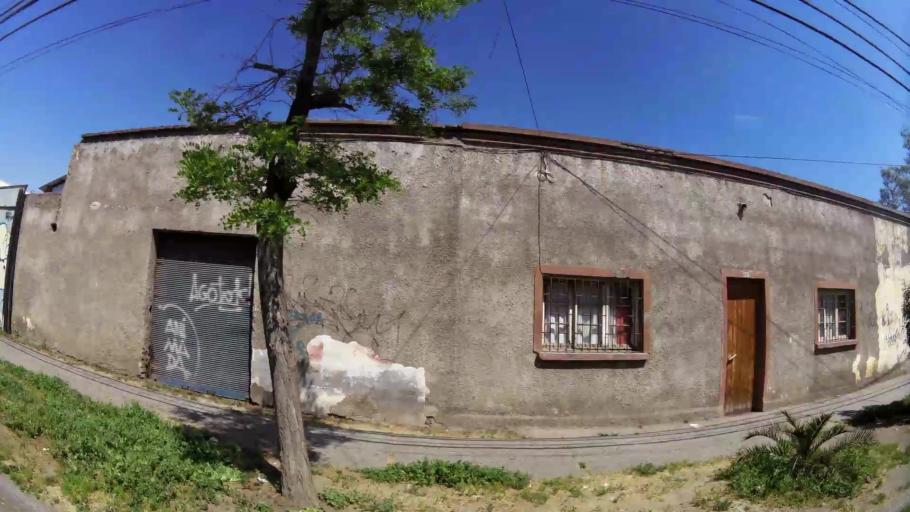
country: CL
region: Santiago Metropolitan
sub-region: Provincia de Santiago
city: La Pintana
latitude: -33.5298
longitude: -70.6517
